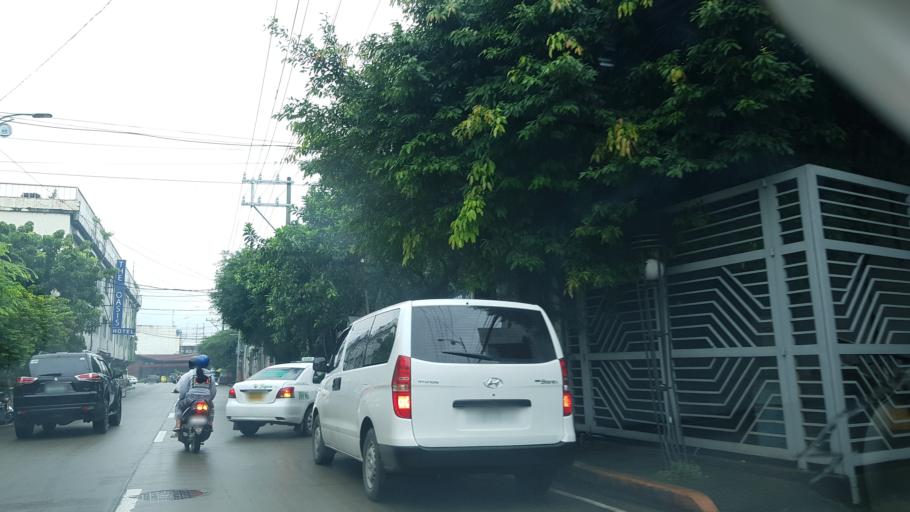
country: PH
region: Metro Manila
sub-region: City of Manila
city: Quiapo
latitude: 14.5804
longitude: 120.9897
